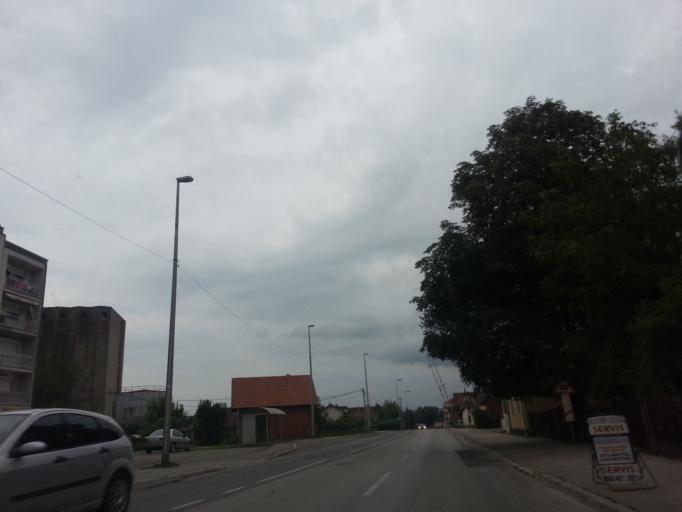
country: BA
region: Brcko
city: Brcko
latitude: 44.8712
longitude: 18.8165
